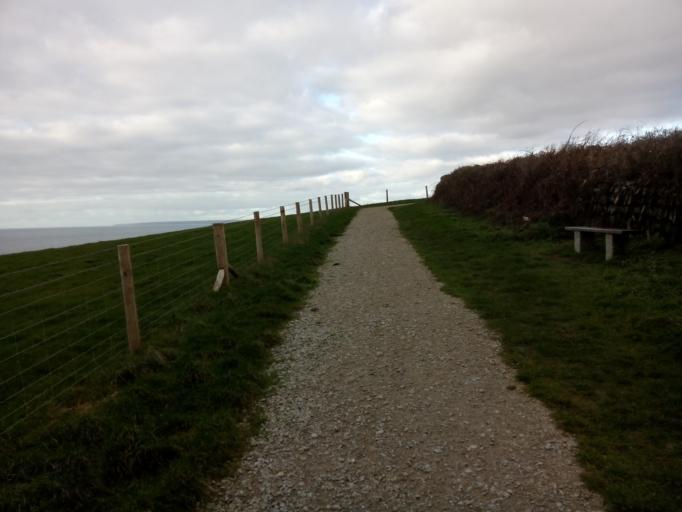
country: GB
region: England
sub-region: Cornwall
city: Porthleven
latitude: 50.0774
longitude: -5.3035
